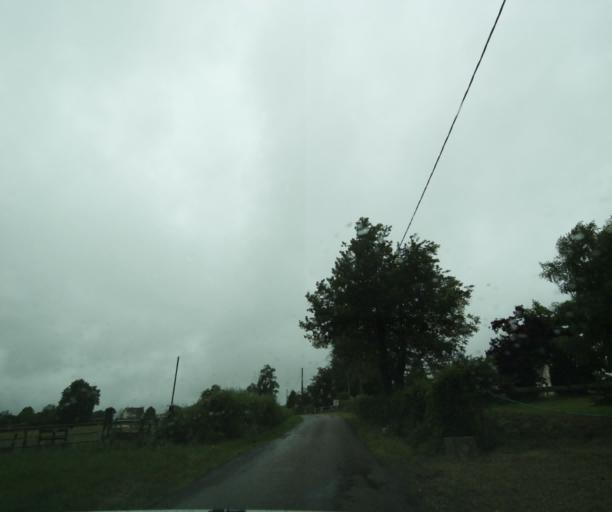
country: FR
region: Bourgogne
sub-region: Departement de Saone-et-Loire
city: Charolles
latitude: 46.4228
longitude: 4.2997
